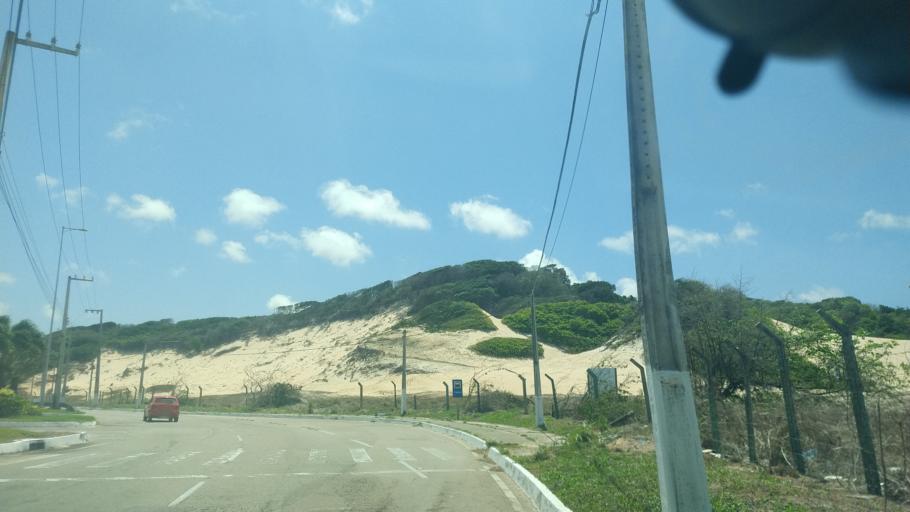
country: BR
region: Rio Grande do Norte
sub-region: Natal
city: Natal
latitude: -5.8312
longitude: -35.1830
